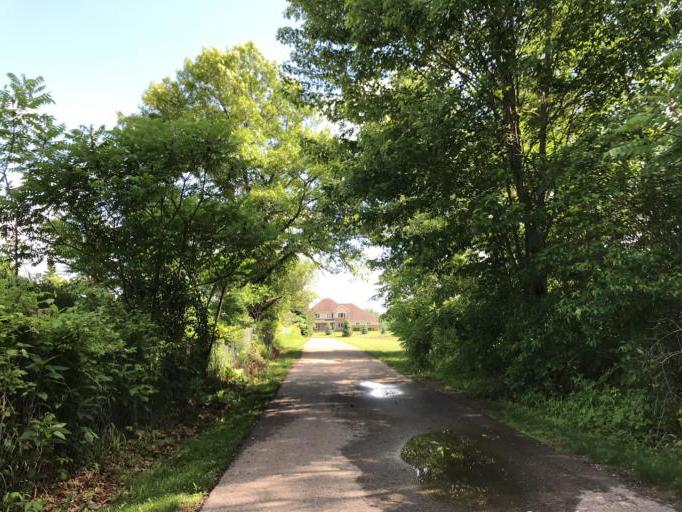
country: US
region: Michigan
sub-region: Oakland County
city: South Lyon
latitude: 42.4328
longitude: -83.6592
